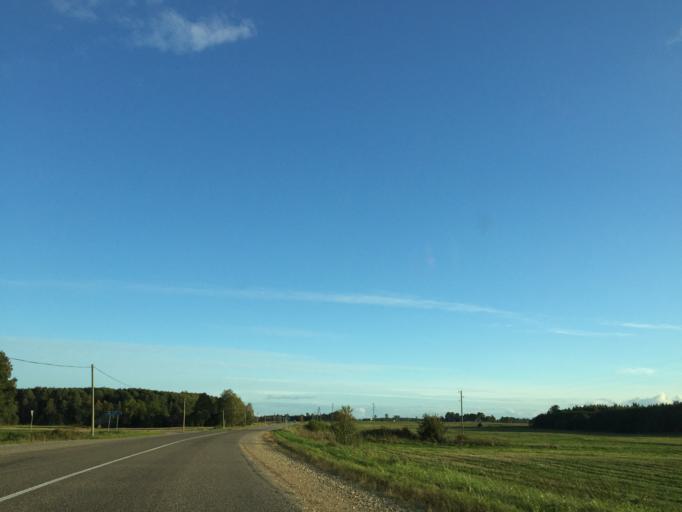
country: LV
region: Saldus Rajons
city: Saldus
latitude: 56.7450
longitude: 22.3774
